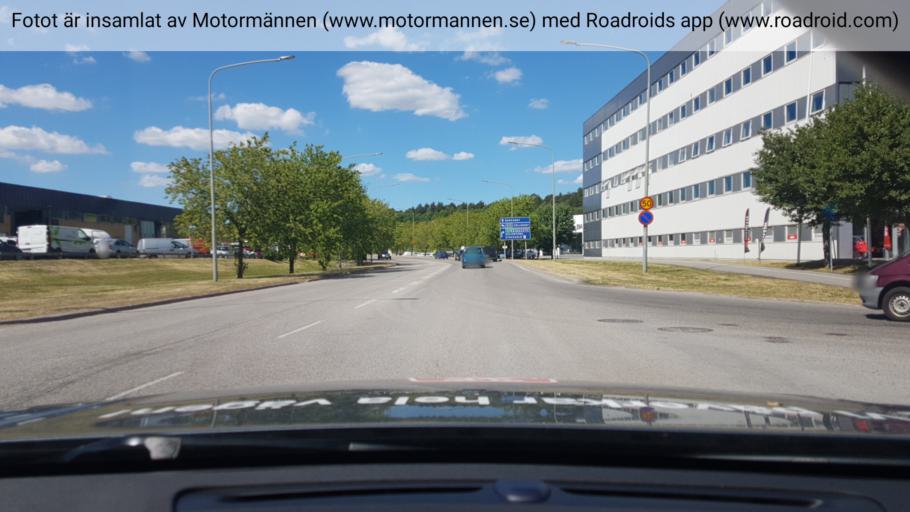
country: SE
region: Stockholm
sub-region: Jarfalla Kommun
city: Jakobsberg
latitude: 59.3904
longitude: 17.8722
